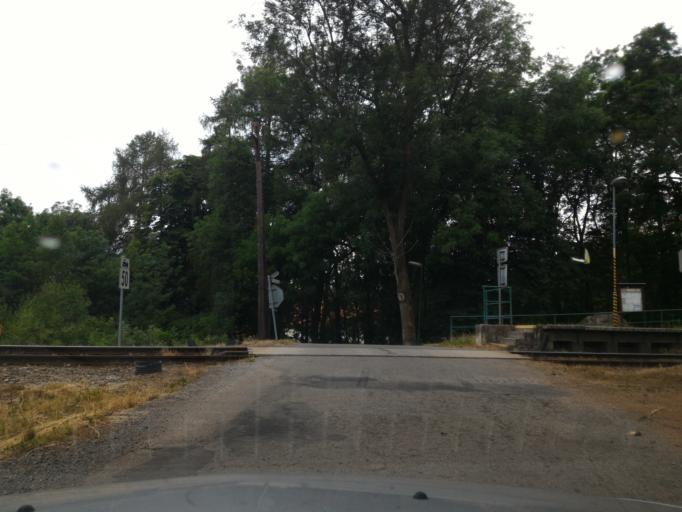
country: CZ
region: Vysocina
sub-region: Okres Jihlava
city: Telc
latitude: 49.1742
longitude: 15.4627
